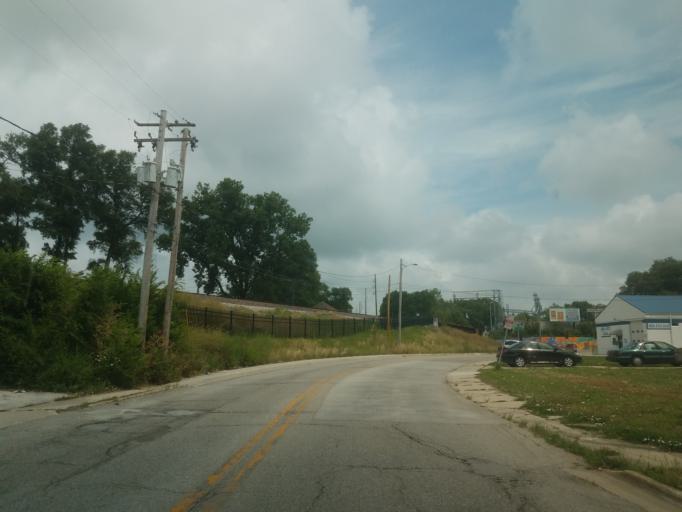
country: US
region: Illinois
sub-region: McLean County
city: Bloomington
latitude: 40.4810
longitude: -89.0066
